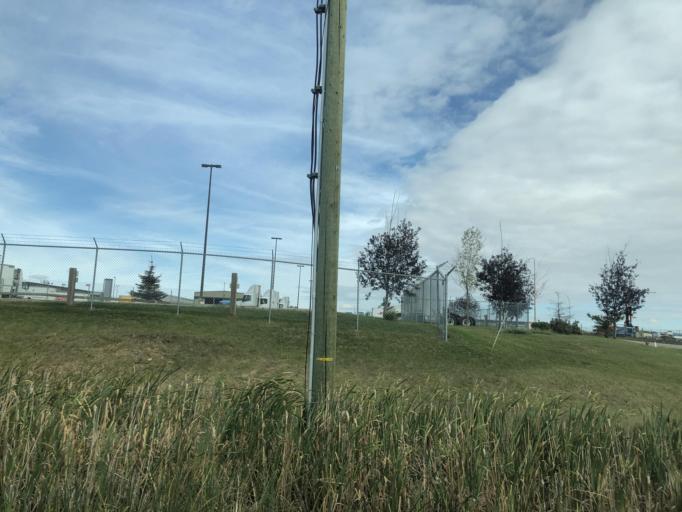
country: CA
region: Alberta
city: Chestermere
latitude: 50.9663
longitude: -113.9085
